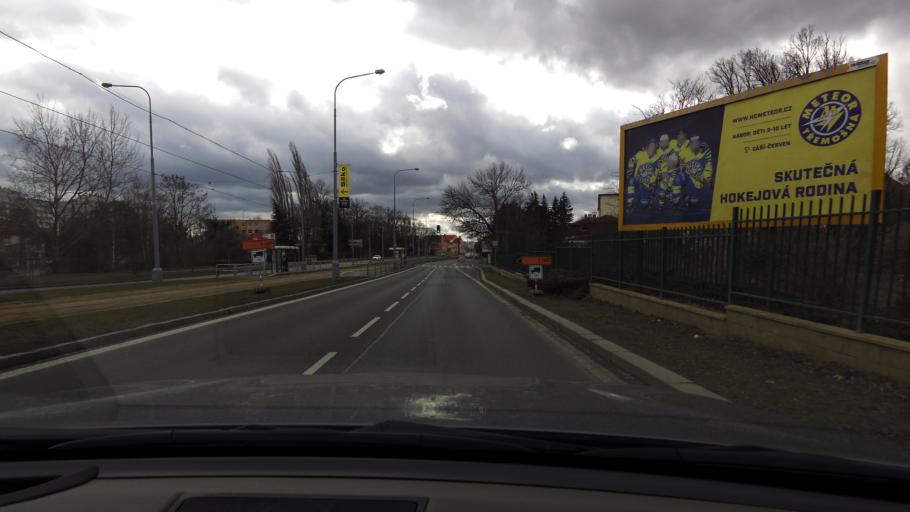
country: CZ
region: Plzensky
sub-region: Okres Plzen-Mesto
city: Pilsen
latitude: 49.7627
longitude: 13.3707
